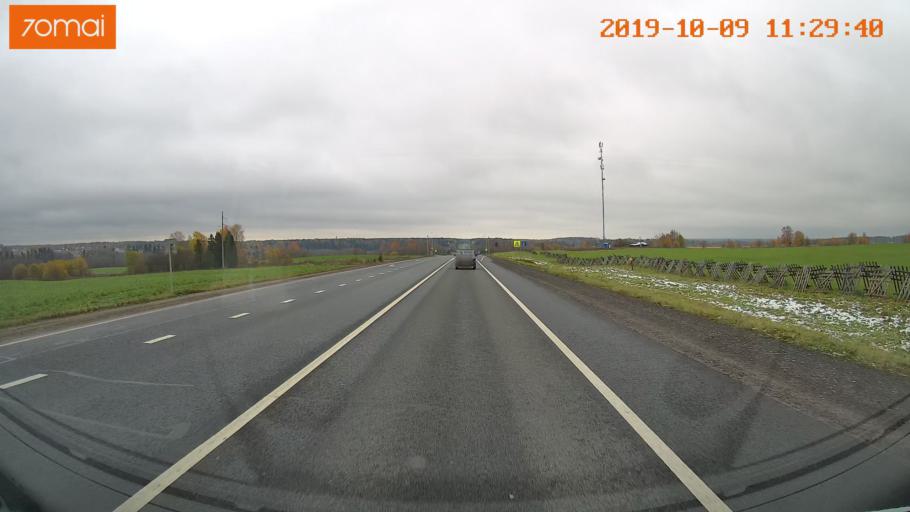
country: RU
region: Vologda
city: Vologda
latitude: 59.0601
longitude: 40.0588
